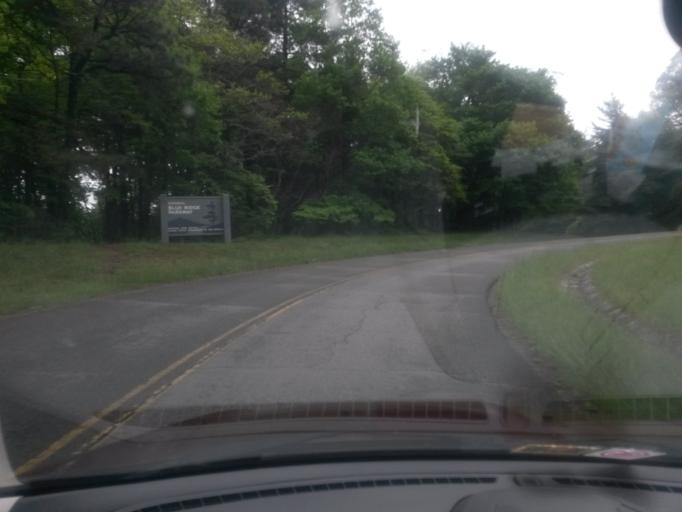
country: US
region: Virginia
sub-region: Floyd County
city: Floyd
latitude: 36.8433
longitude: -80.3205
